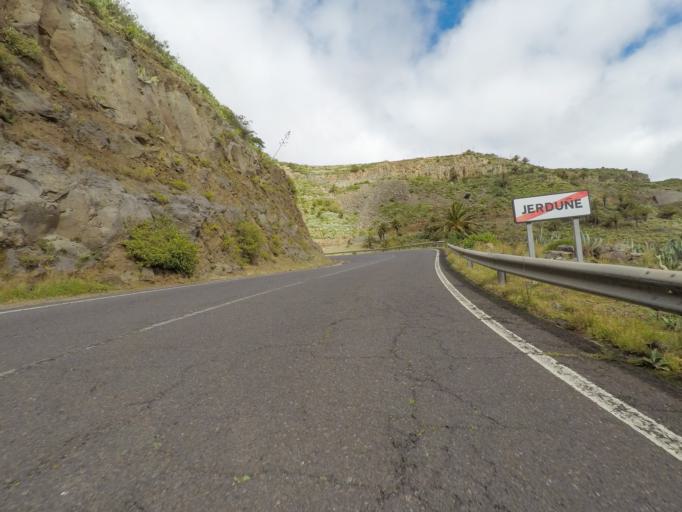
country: ES
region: Canary Islands
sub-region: Provincia de Santa Cruz de Tenerife
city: Alajero
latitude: 28.0970
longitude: -17.1905
